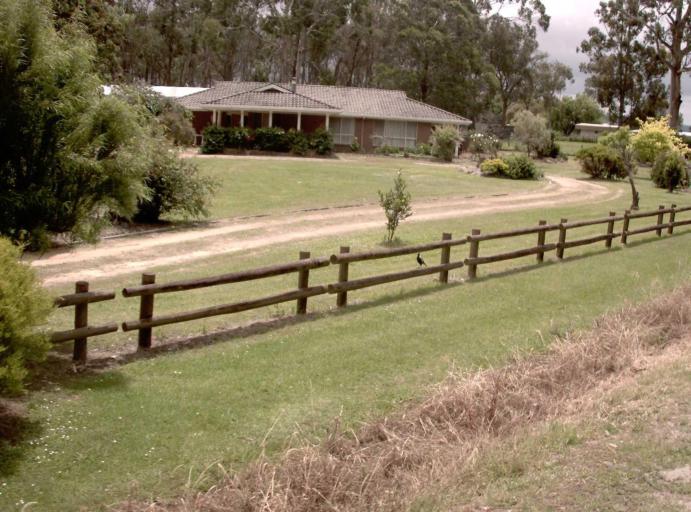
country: AU
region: Victoria
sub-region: Latrobe
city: Traralgon
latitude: -38.5410
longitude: 146.6566
